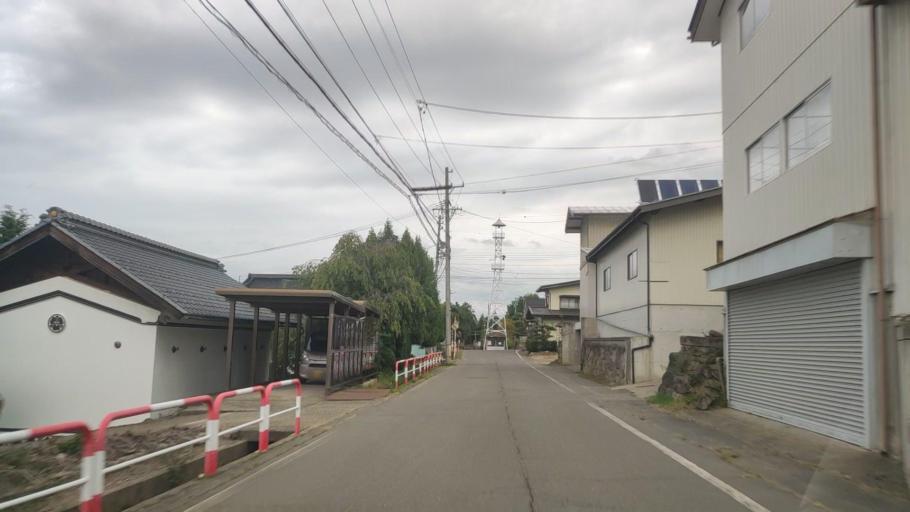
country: JP
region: Nagano
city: Nakano
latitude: 36.7855
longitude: 138.3670
